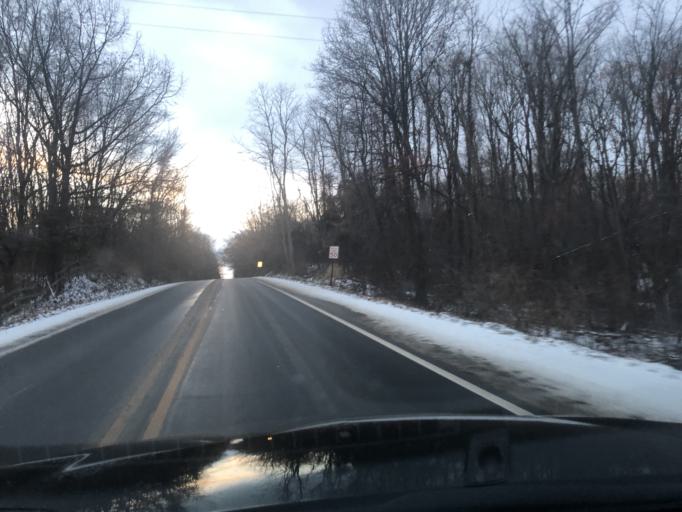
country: US
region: Michigan
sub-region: Oakland County
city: Milford
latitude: 42.5787
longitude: -83.6397
